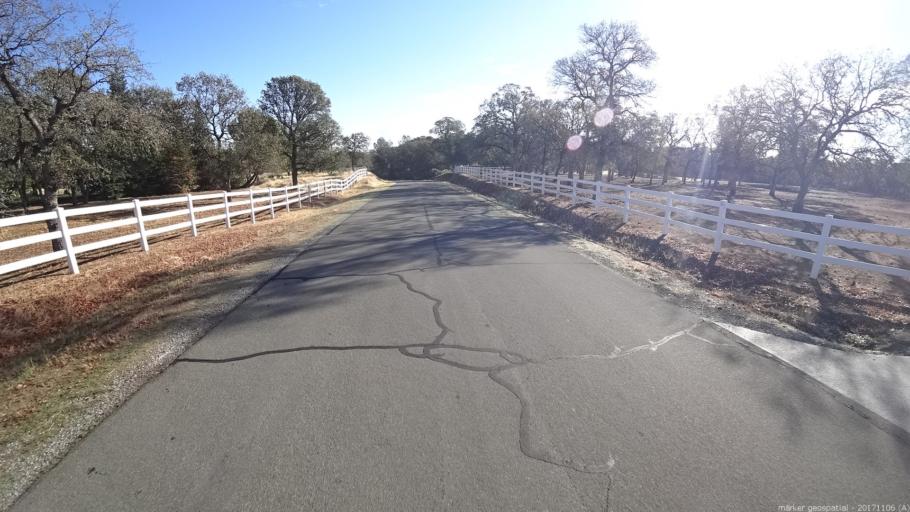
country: US
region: California
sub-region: Shasta County
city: Palo Cedro
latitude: 40.5029
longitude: -122.2423
